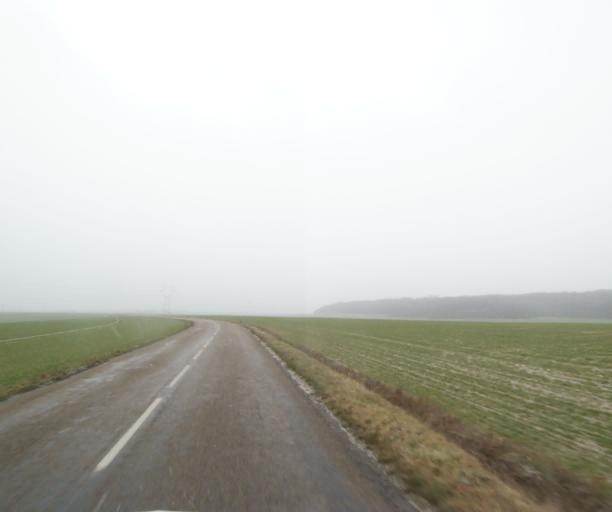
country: FR
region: Champagne-Ardenne
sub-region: Departement de la Haute-Marne
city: Bienville
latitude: 48.5200
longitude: 5.0283
